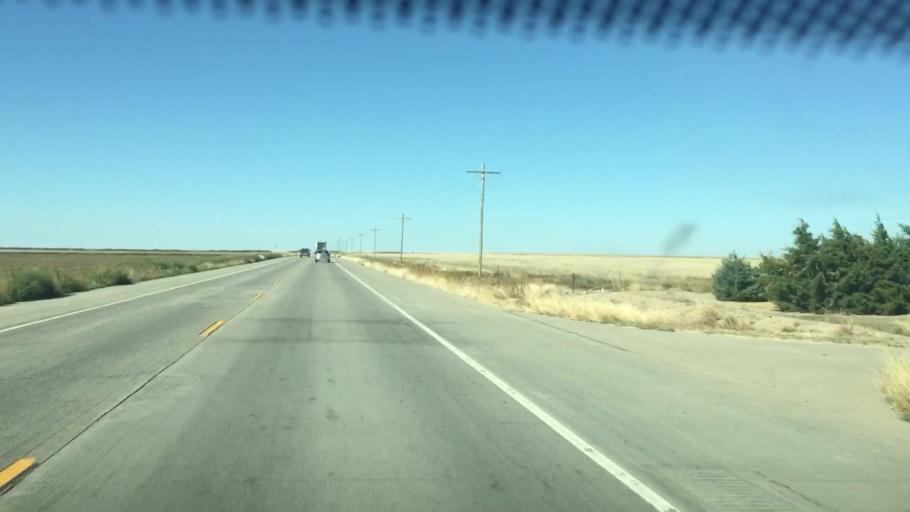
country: US
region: Colorado
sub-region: Prowers County
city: Lamar
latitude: 38.2316
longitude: -102.7240
